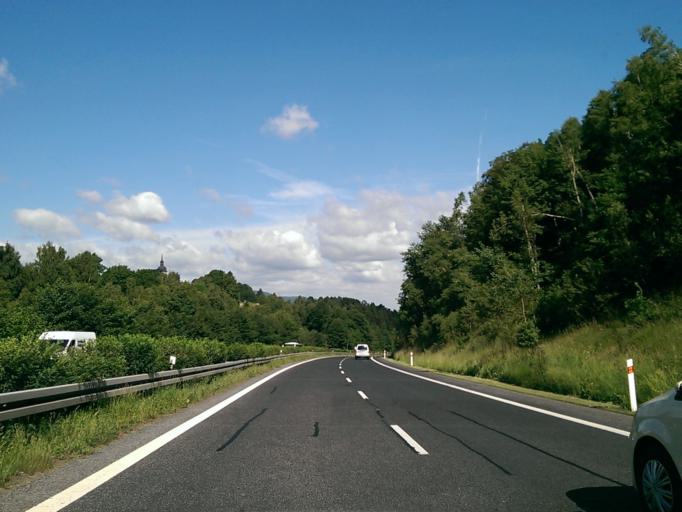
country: CZ
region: Liberecky
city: Hodkovice nad Mohelkou
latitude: 50.7115
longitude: 15.0813
